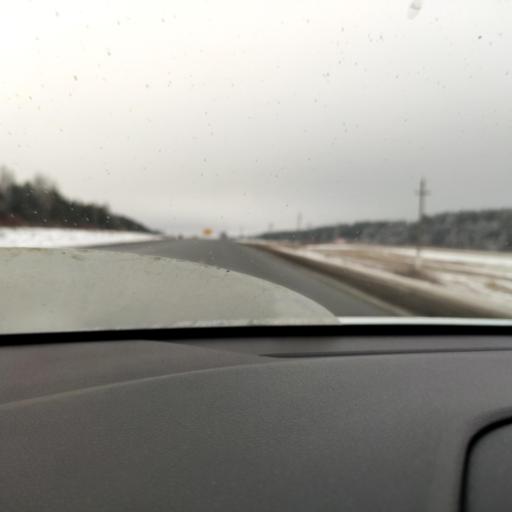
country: RU
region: Tatarstan
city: Sviyazhsk
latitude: 55.7303
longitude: 48.8053
